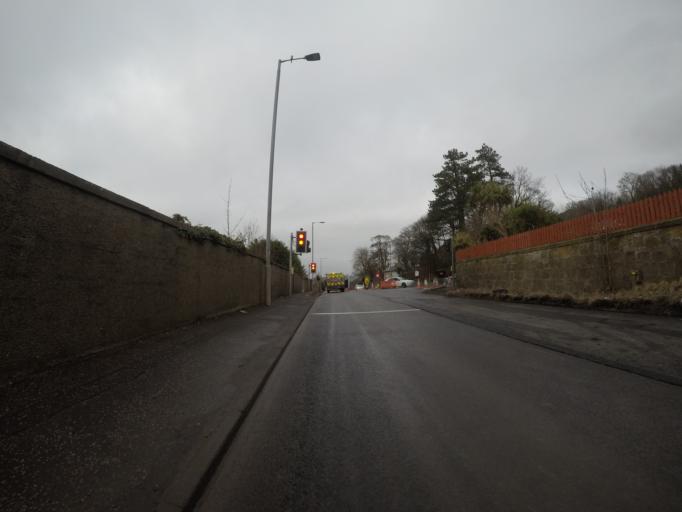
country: GB
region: Scotland
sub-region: North Ayrshire
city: Largs
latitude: 55.7847
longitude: -4.8579
